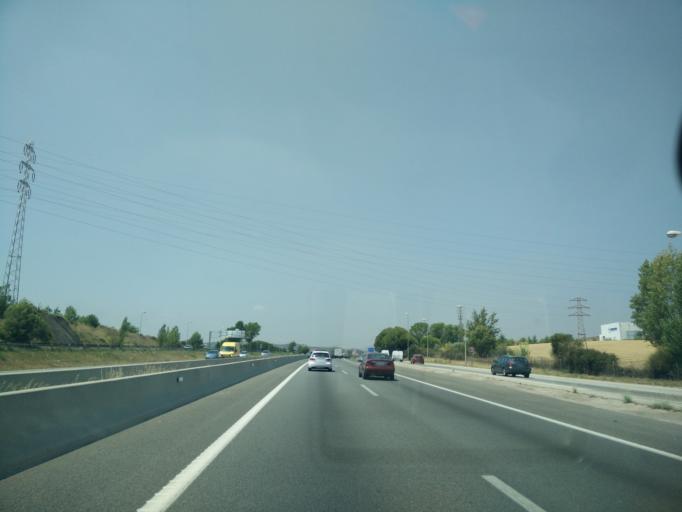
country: ES
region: Catalonia
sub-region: Provincia de Barcelona
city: Sant Quirze del Valles
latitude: 41.5427
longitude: 2.0493
